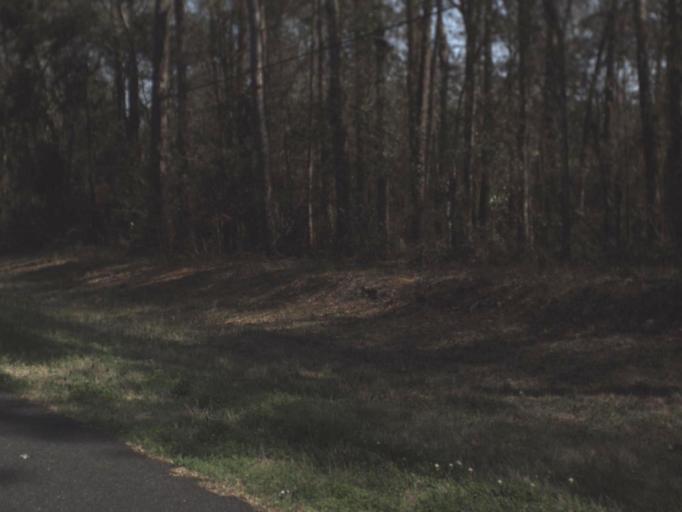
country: US
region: Florida
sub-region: Gadsden County
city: Havana
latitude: 30.6103
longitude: -84.4236
